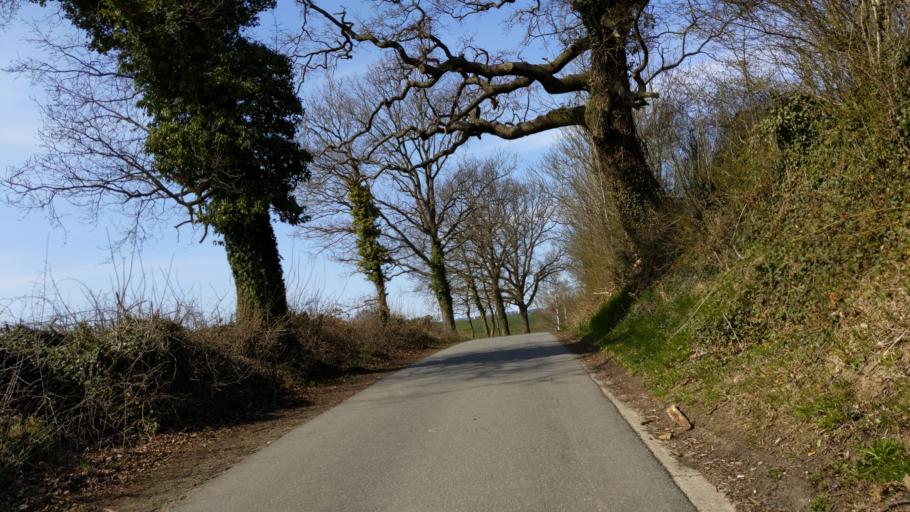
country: DE
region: Schleswig-Holstein
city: Schashagen
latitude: 54.1295
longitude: 10.8859
